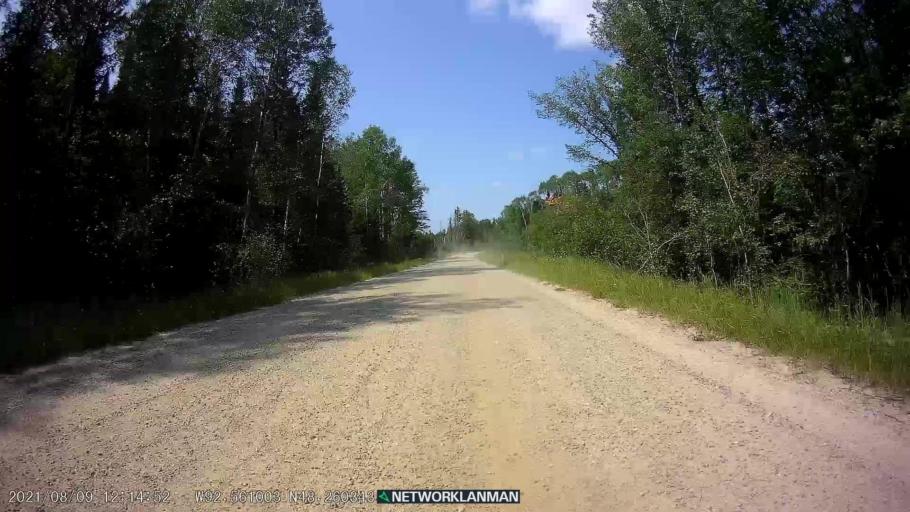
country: US
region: Minnesota
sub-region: Saint Louis County
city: Parkville
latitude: 48.2602
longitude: -92.5608
